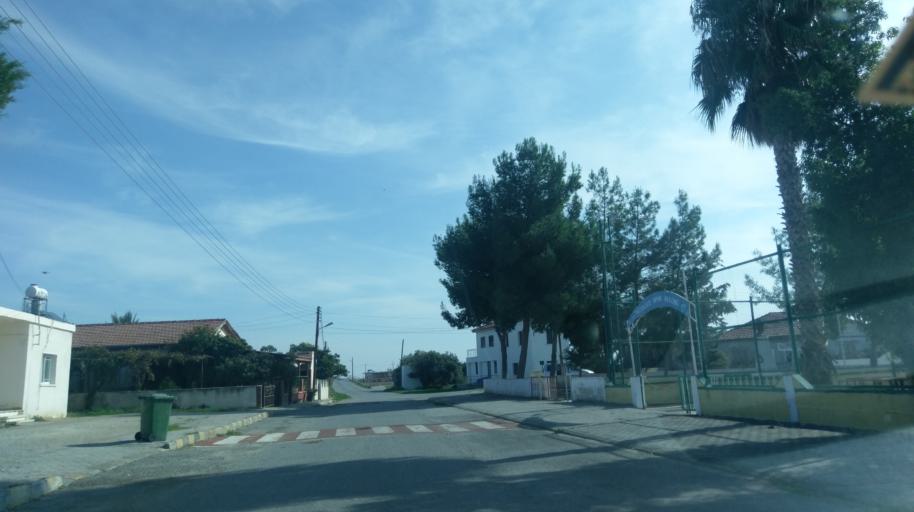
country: CY
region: Ammochostos
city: Lefkonoiko
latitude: 35.2550
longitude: 33.6882
